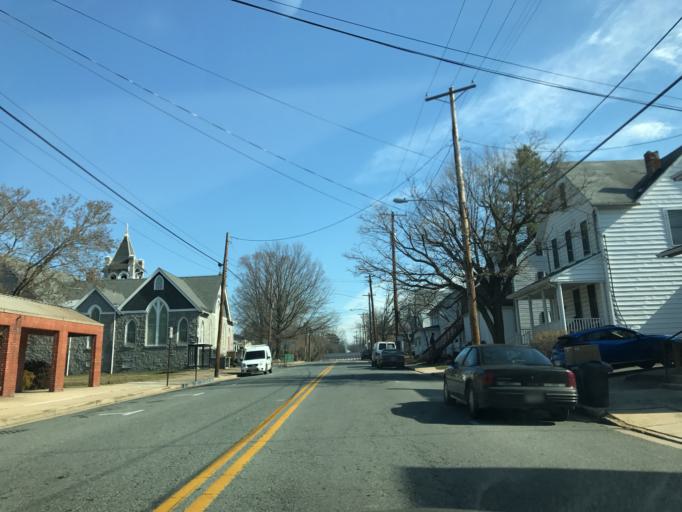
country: US
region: Maryland
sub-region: Cecil County
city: Perryville
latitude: 39.5580
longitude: -76.0758
